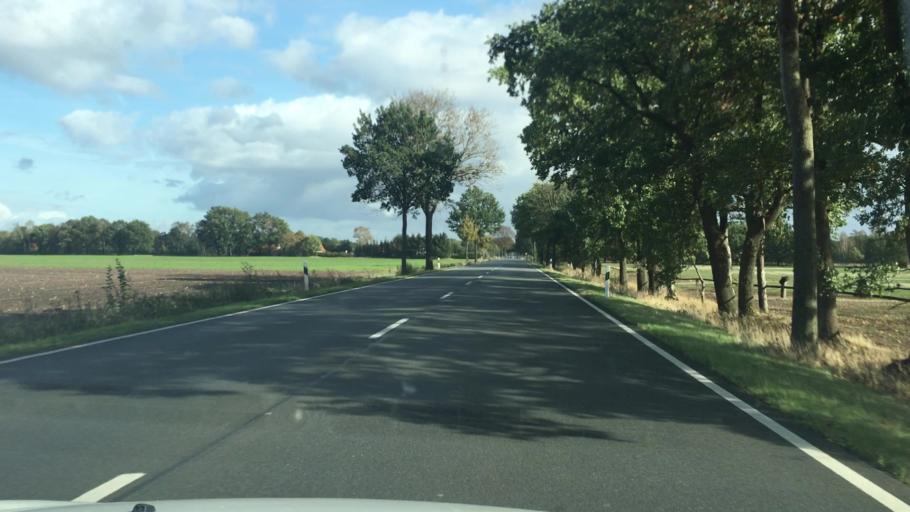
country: DE
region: Lower Saxony
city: Barver
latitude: 52.6096
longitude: 8.5727
